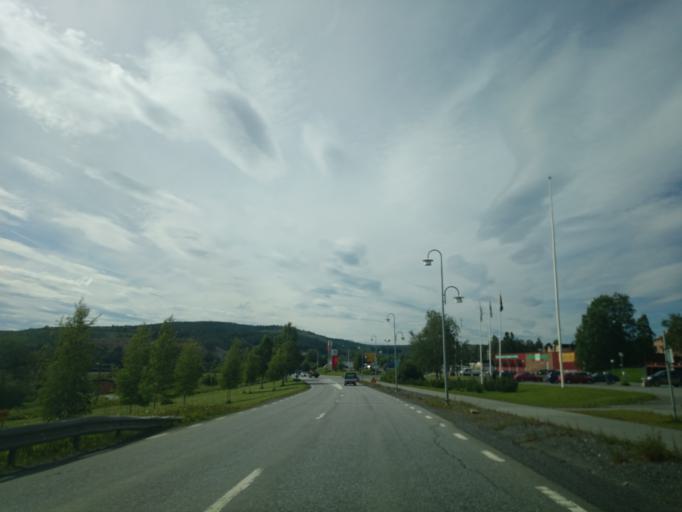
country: SE
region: Jaemtland
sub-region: Are Kommun
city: Jarpen
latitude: 63.3449
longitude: 13.4659
